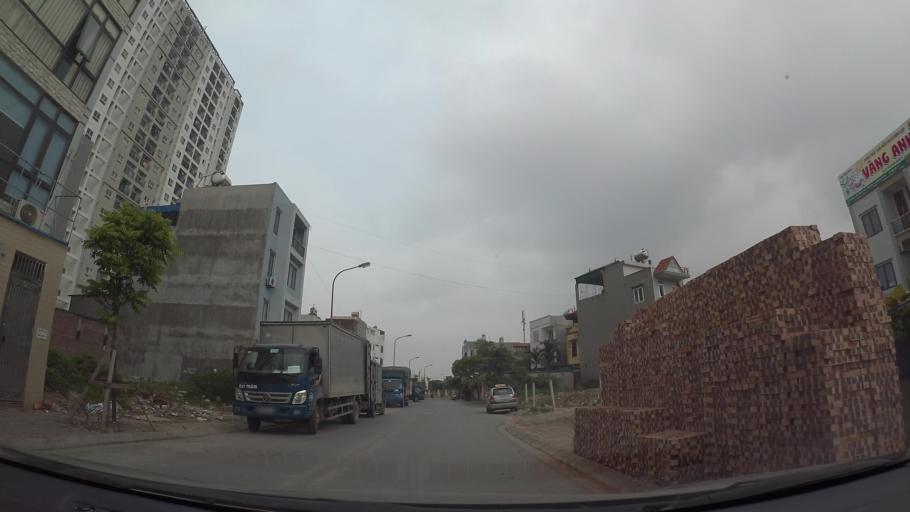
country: VN
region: Ha Noi
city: Trau Quy
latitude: 21.0412
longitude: 105.9283
